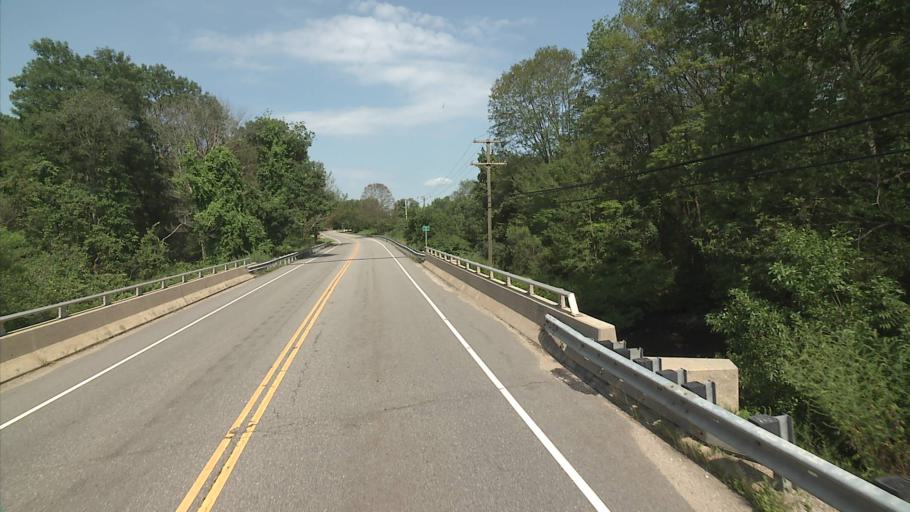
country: US
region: Connecticut
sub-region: New London County
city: Montville Center
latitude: 41.5700
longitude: -72.1756
